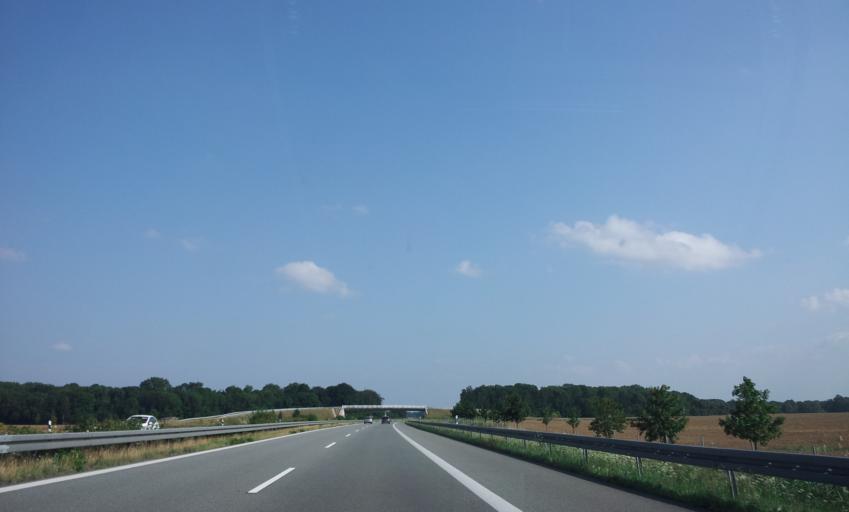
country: DE
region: Mecklenburg-Vorpommern
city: Jarmen
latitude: 53.9835
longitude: 13.3488
